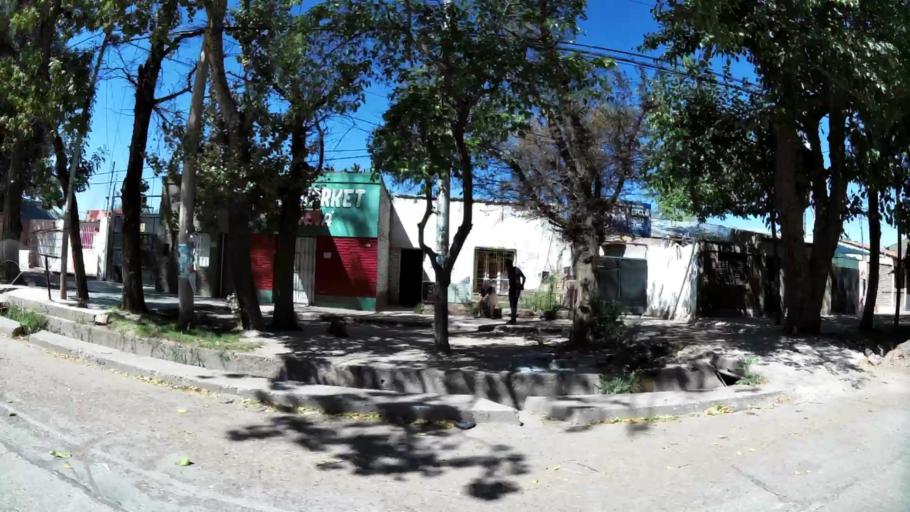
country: AR
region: Mendoza
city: Las Heras
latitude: -32.8396
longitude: -68.8336
